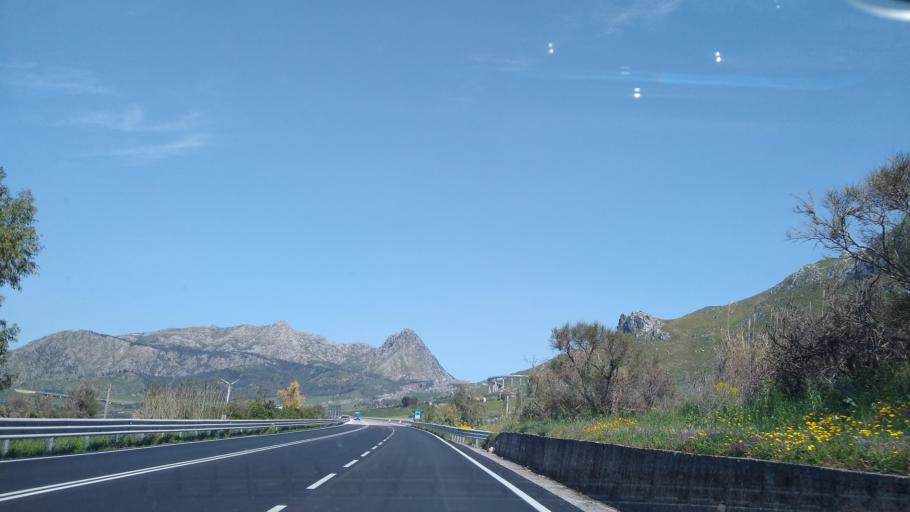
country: IT
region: Sicily
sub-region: Palermo
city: San Giuseppe Jato
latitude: 37.9748
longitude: 13.2098
